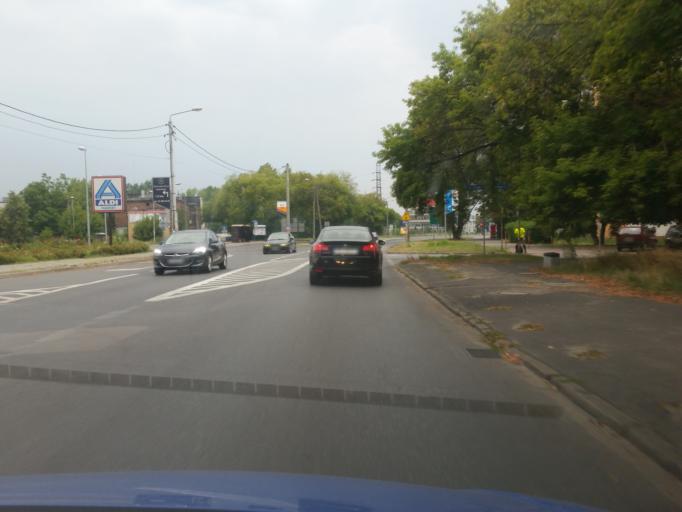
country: PL
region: Silesian Voivodeship
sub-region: Sosnowiec
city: Sosnowiec
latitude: 50.2884
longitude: 19.1138
